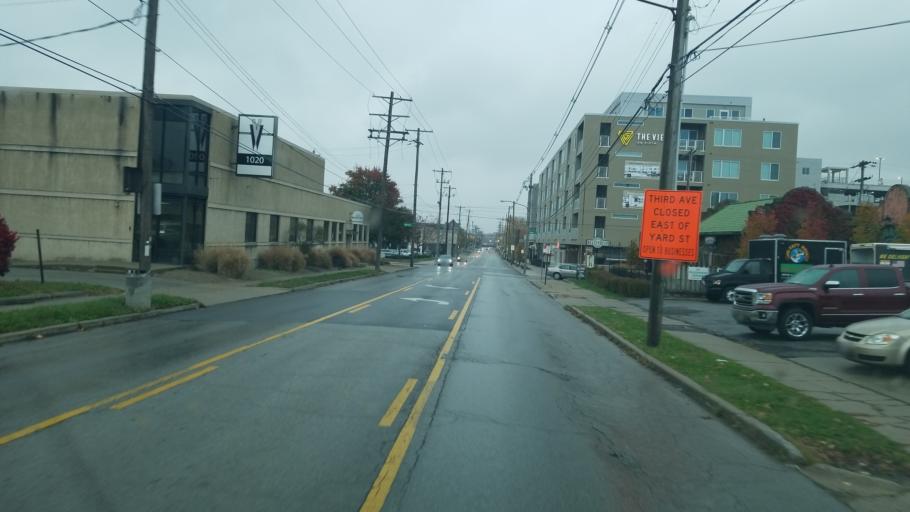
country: US
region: Ohio
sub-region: Franklin County
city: Grandview Heights
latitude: 39.9883
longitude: -83.0342
